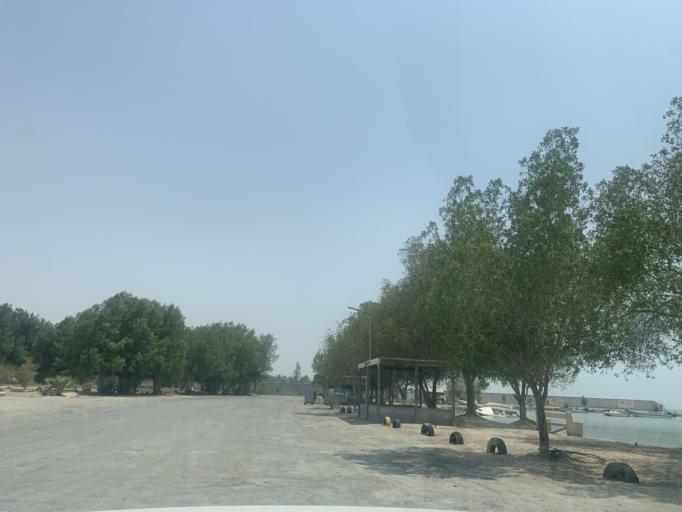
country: BH
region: Central Governorate
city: Madinat Hamad
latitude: 26.1235
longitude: 50.4616
